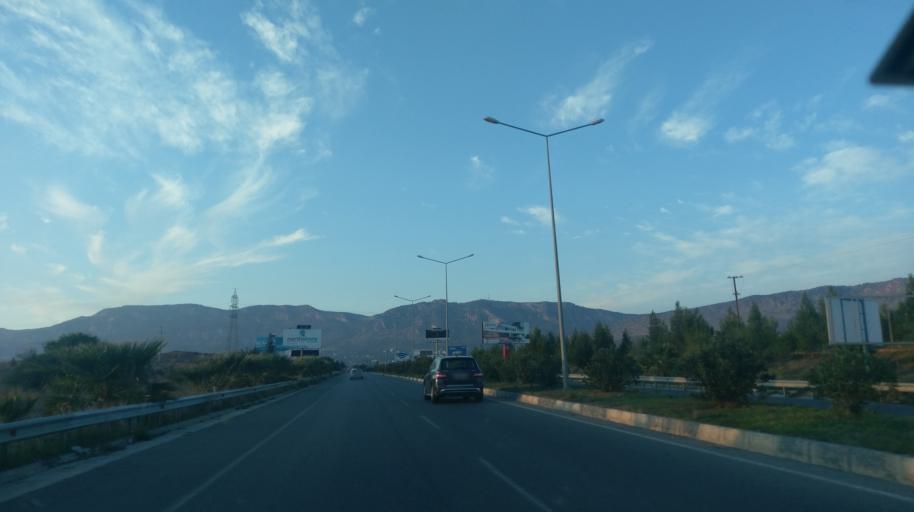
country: CY
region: Keryneia
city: Kyrenia
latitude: 35.2595
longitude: 33.2975
